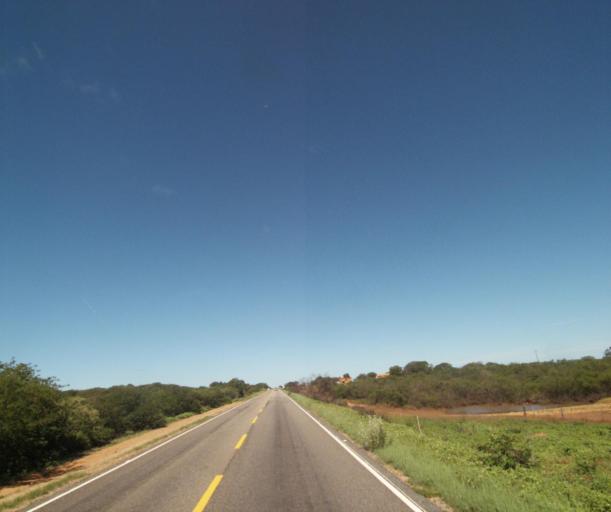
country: BR
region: Bahia
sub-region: Palmas De Monte Alto
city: Palmas de Monte Alto
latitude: -14.2466
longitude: -43.1262
